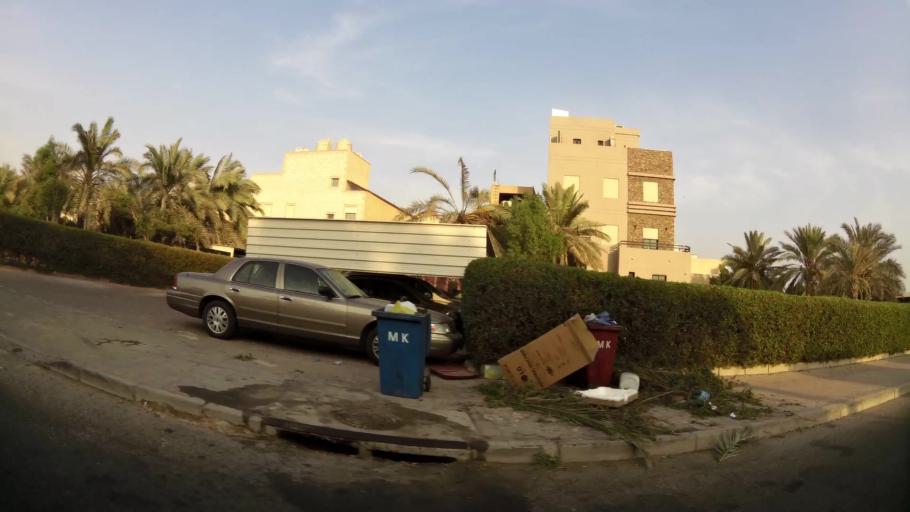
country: KW
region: Mubarak al Kabir
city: Sabah as Salim
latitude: 29.2544
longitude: 48.0710
